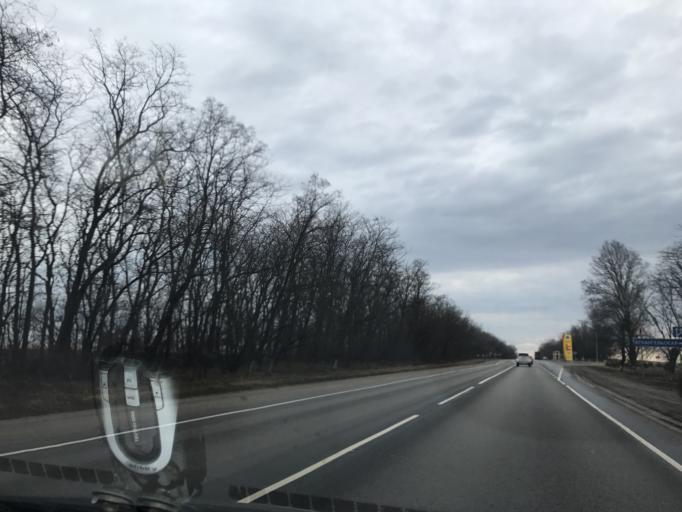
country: RU
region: Krasnodarskiy
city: Alekseyevskaya
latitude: 45.6927
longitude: 40.3038
